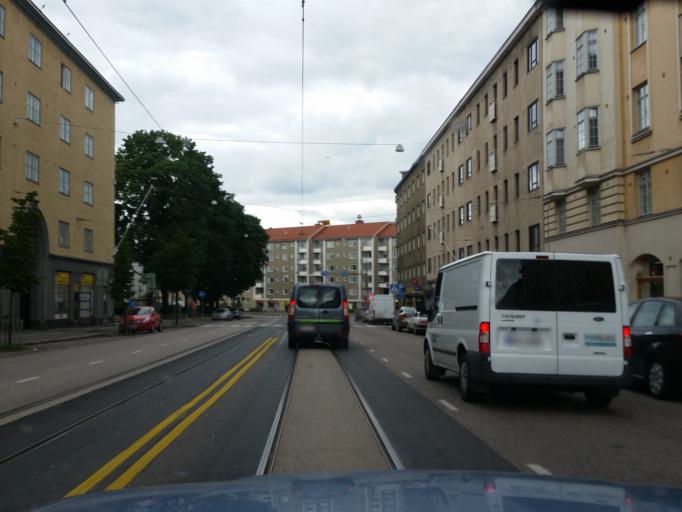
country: FI
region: Uusimaa
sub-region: Helsinki
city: Helsinki
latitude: 60.1961
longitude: 24.9603
